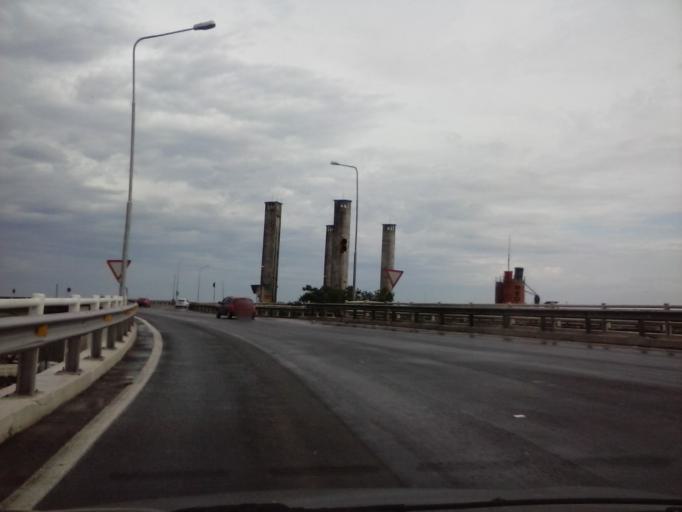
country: BR
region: Rio Grande do Sul
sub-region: Porto Alegre
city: Porto Alegre
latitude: -29.9975
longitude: -51.2062
